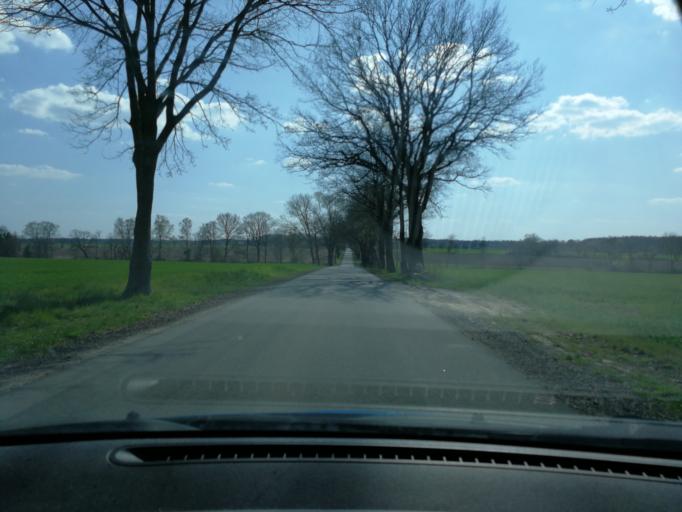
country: DE
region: Lower Saxony
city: Reinstorf
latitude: 53.2122
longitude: 10.5866
